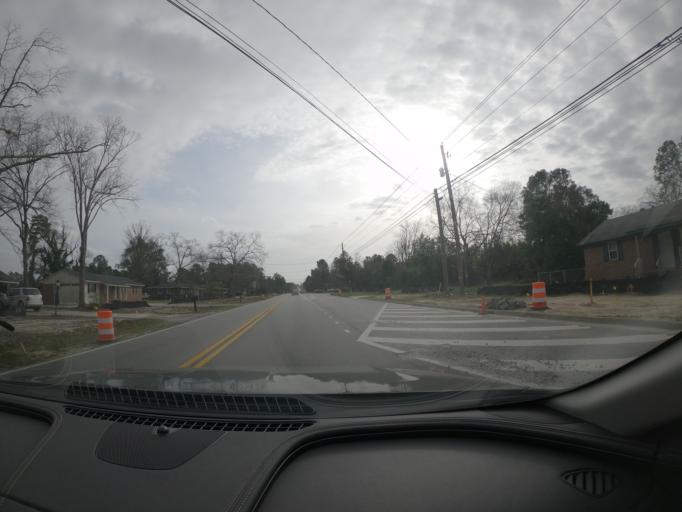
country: US
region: Georgia
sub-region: Columbia County
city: Martinez
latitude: 33.5052
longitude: -82.1063
